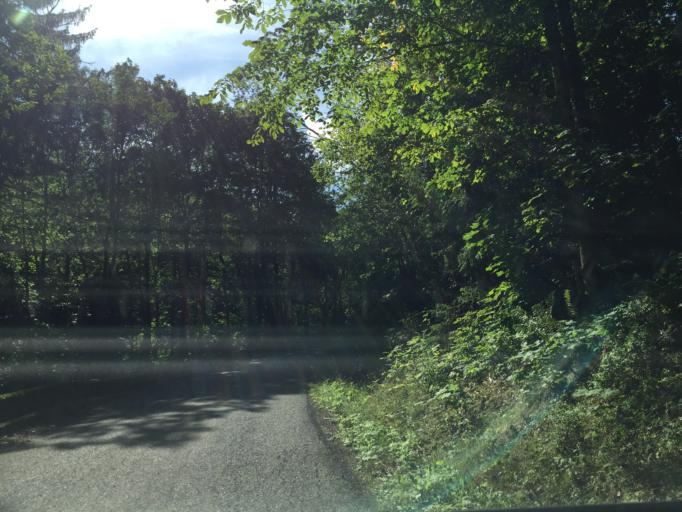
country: NO
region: Vestfold
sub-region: Hof
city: Hof
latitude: 59.4828
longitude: 10.1501
